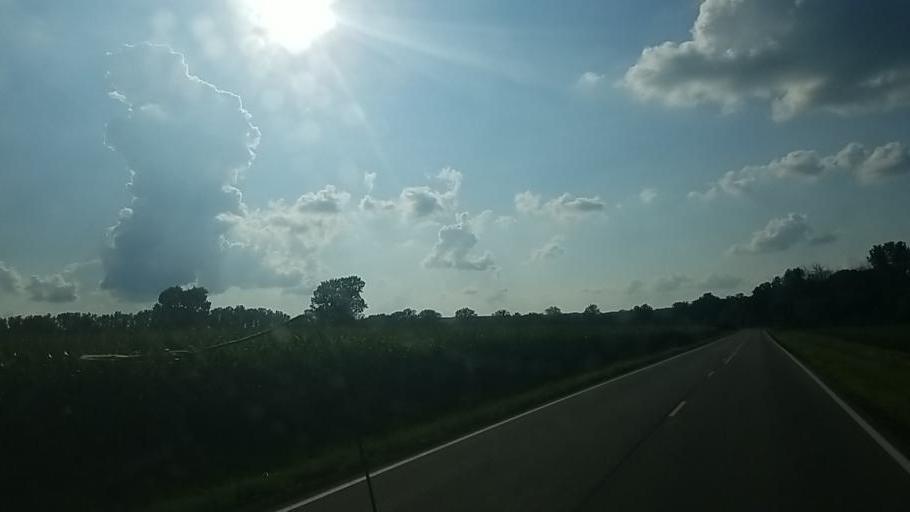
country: US
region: Ohio
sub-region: Wayne County
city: West Salem
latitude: 40.8926
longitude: -82.1427
